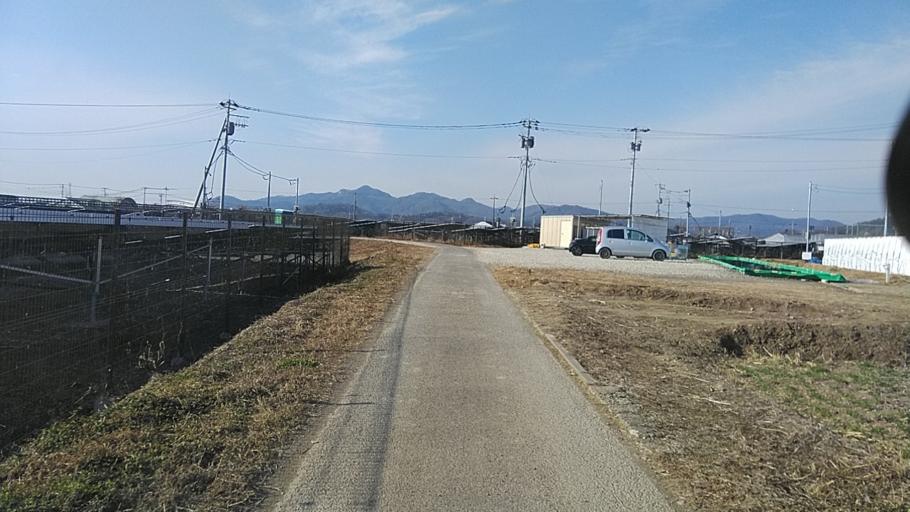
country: JP
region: Tochigi
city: Tanuma
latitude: 36.3519
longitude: 139.5607
